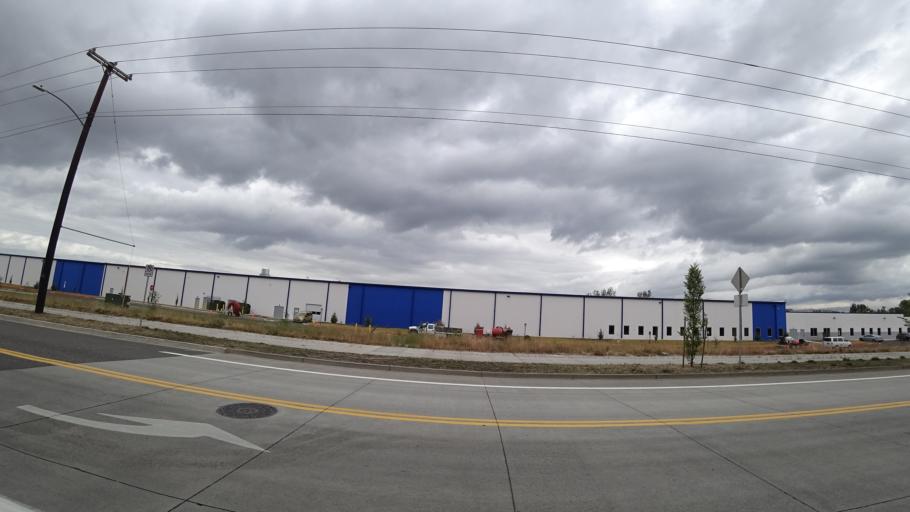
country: US
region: Washington
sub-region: Clark County
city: Walnut Grove
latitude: 45.5736
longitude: -122.5873
